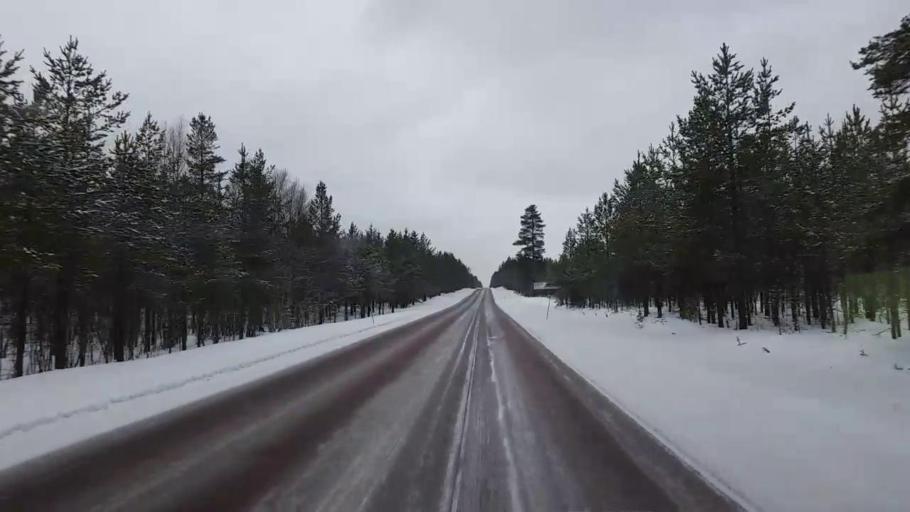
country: SE
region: Jaemtland
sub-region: Bergs Kommun
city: Hoverberg
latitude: 62.4384
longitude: 14.5837
